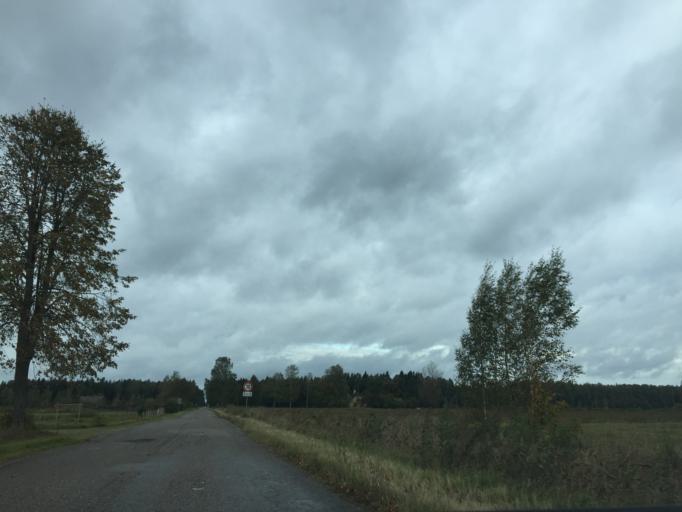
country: LV
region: Olaine
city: Olaine
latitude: 56.7694
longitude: 23.8746
